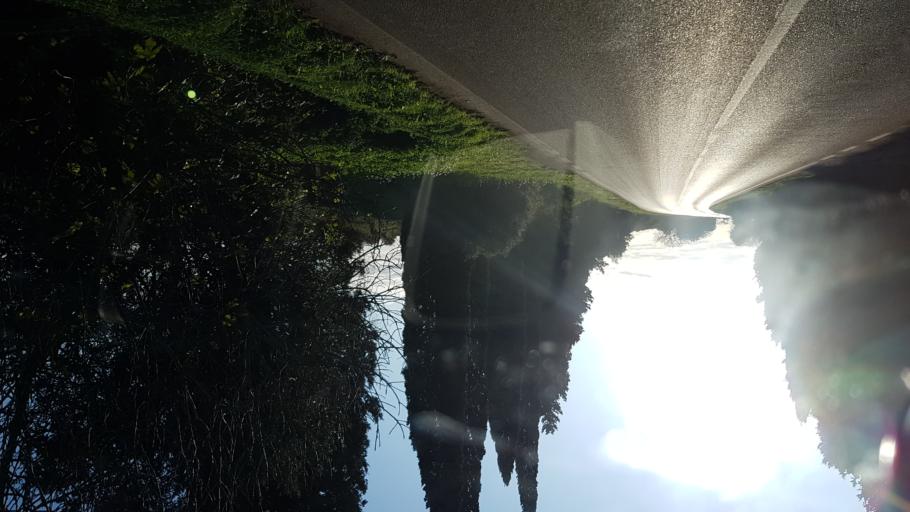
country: IT
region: Apulia
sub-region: Provincia di Brindisi
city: Torchiarolo
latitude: 40.5463
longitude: 18.0439
